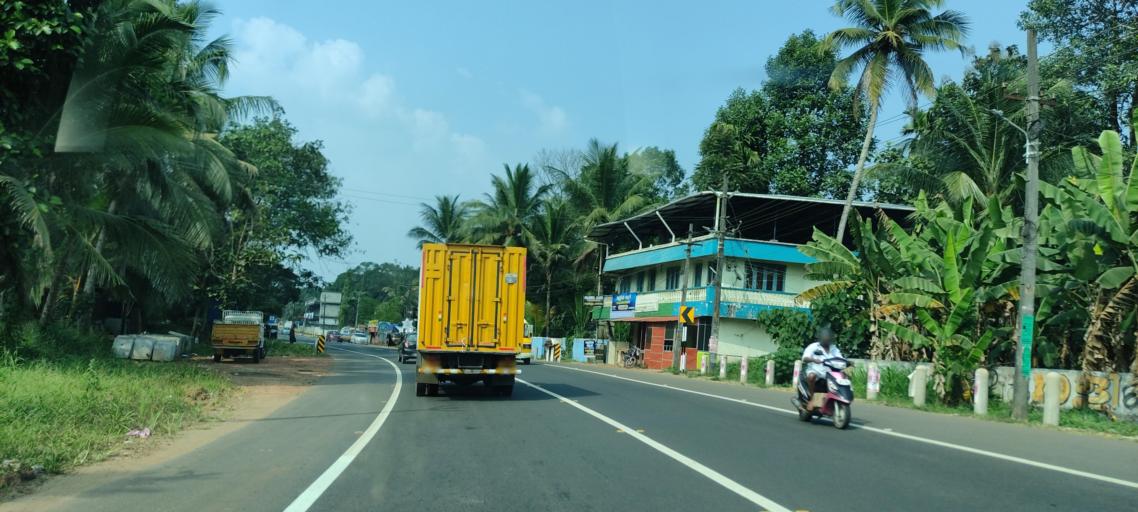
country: IN
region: Kerala
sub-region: Alappuzha
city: Chengannur
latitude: 9.2787
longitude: 76.6558
